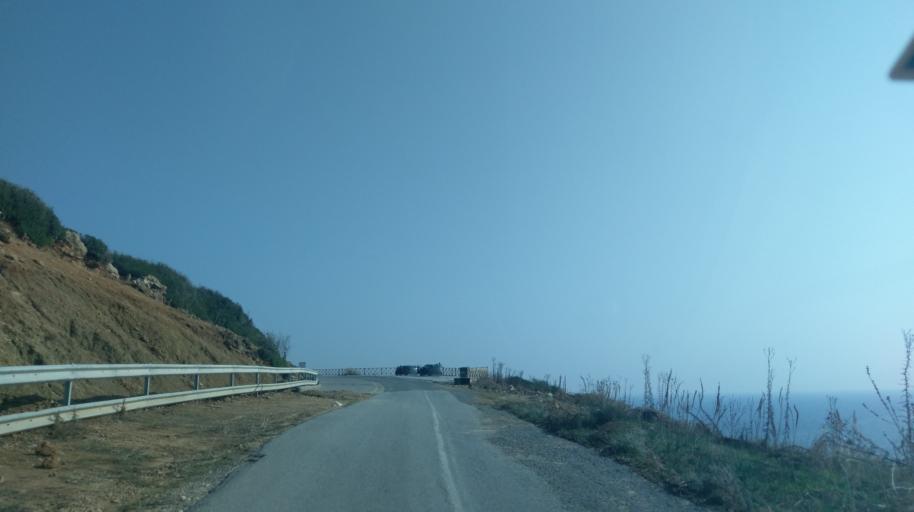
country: CY
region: Ammochostos
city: Rizokarpaso
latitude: 35.6442
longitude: 34.5571
